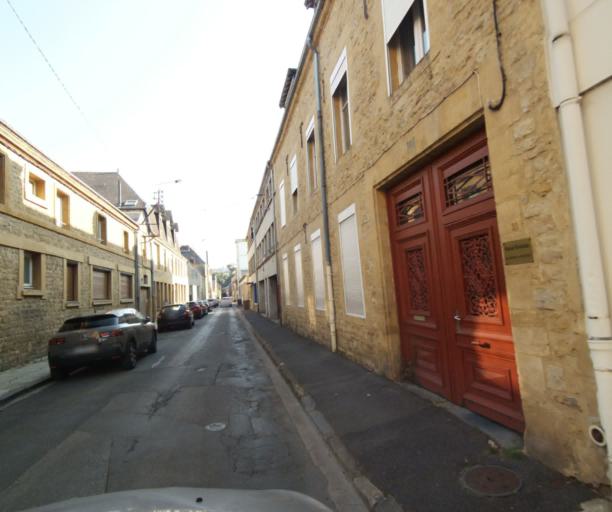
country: FR
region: Champagne-Ardenne
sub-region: Departement des Ardennes
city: Charleville-Mezieres
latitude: 49.7717
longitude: 4.7245
